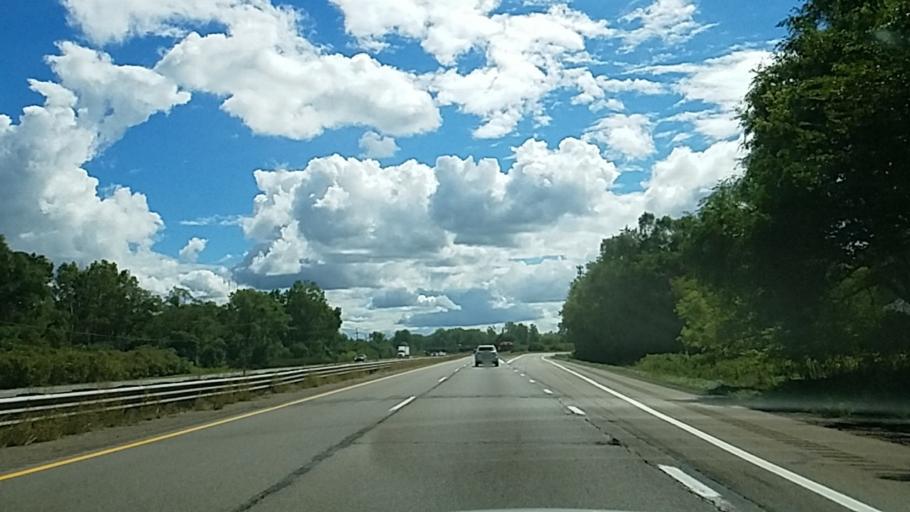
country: US
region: Michigan
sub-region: Livingston County
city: Whitmore Lake
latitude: 42.3994
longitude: -83.7633
